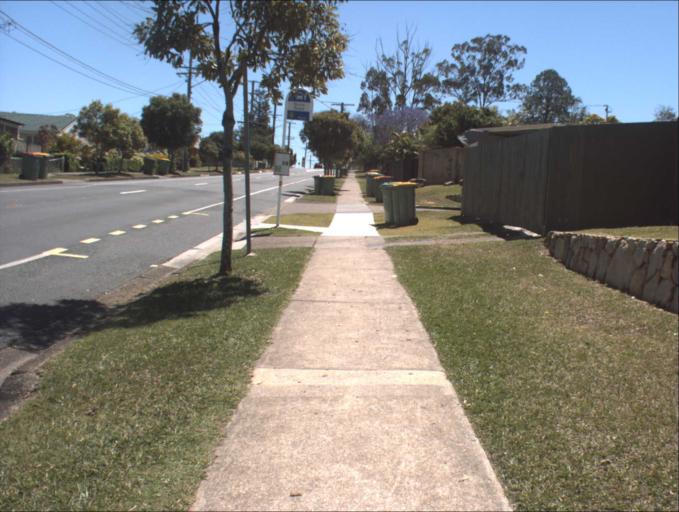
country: AU
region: Queensland
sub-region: Logan
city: Woodridge
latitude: -27.6300
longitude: 153.1034
